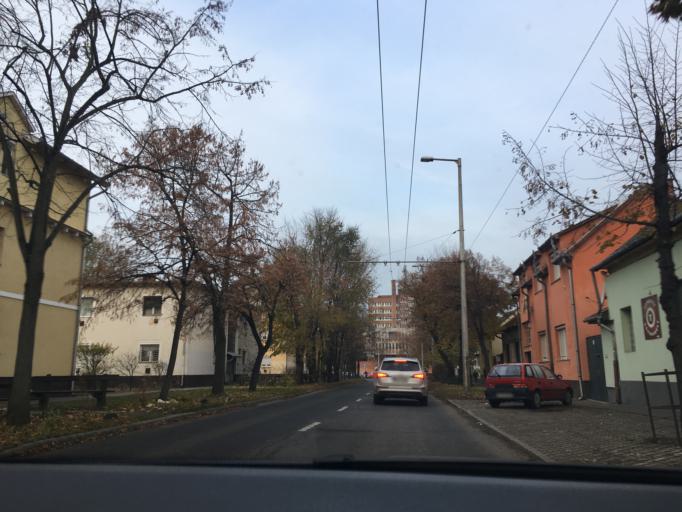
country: HU
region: Hajdu-Bihar
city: Debrecen
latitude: 47.5360
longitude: 21.6435
